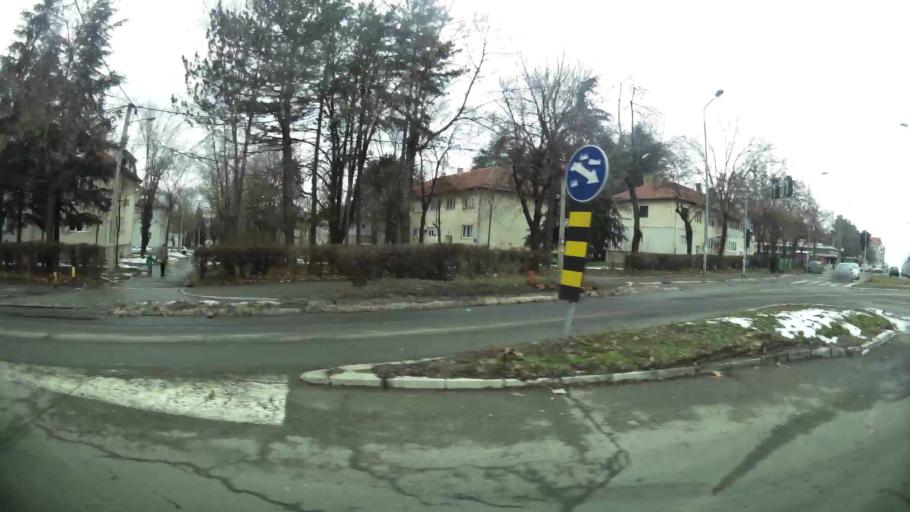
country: RS
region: Central Serbia
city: Sremcica
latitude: 44.7284
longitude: 20.3748
